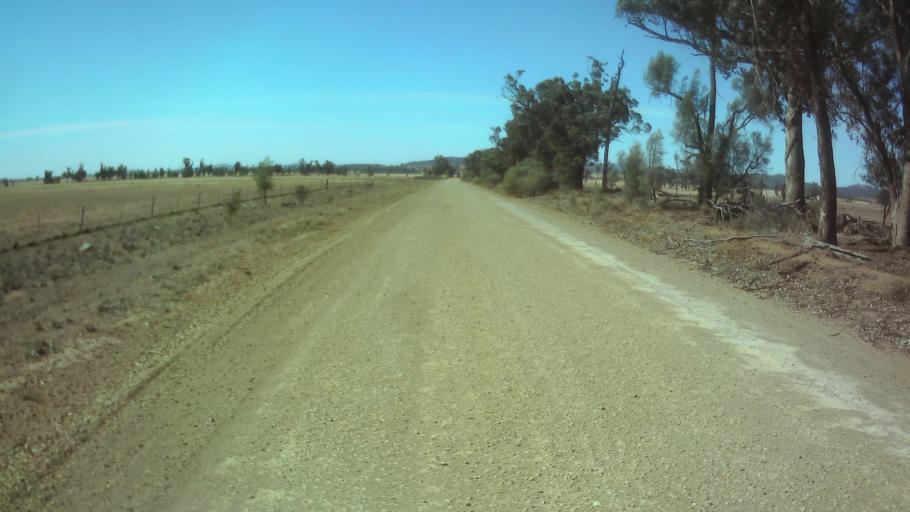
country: AU
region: New South Wales
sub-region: Forbes
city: Forbes
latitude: -33.7118
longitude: 147.7472
